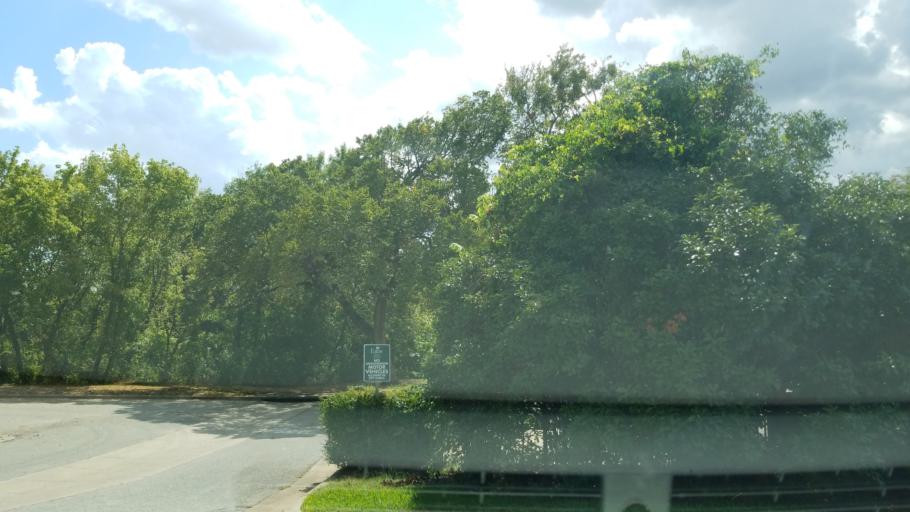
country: US
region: Texas
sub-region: Tarrant County
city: Euless
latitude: 32.8668
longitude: -97.0765
